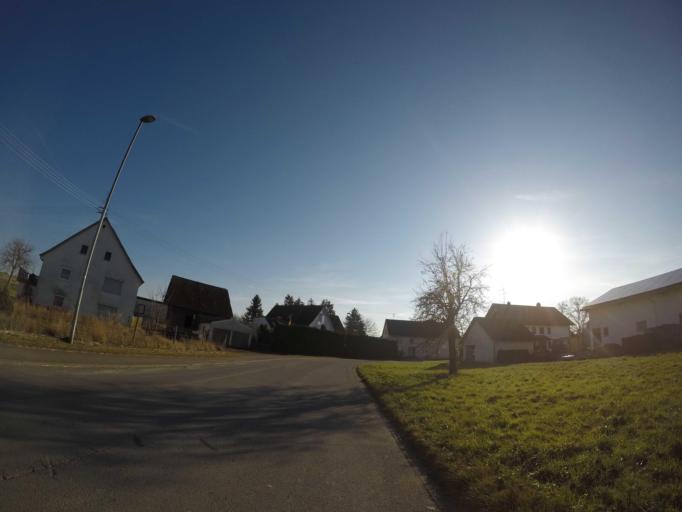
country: DE
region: Baden-Wuerttemberg
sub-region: Tuebingen Region
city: Grundsheim
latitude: 48.1760
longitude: 9.6677
